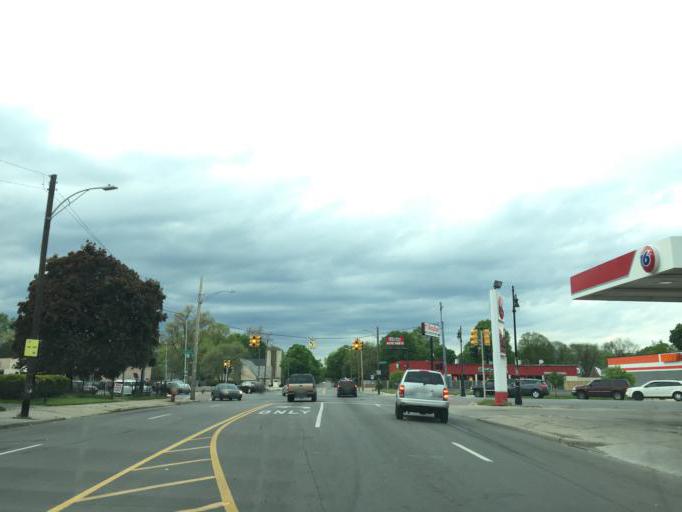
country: US
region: Michigan
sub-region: Wayne County
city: Redford
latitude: 42.4079
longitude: -83.2377
